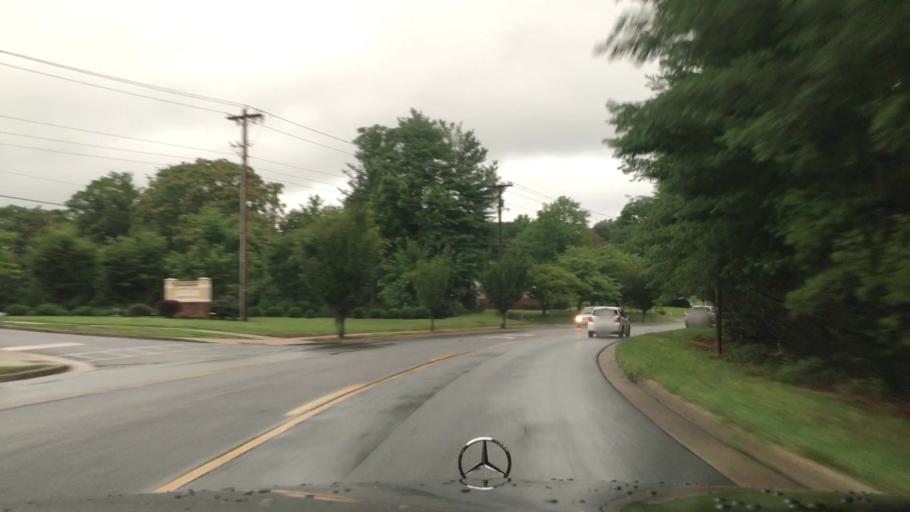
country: US
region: Virginia
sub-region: Campbell County
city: Timberlake
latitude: 37.3606
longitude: -79.2295
